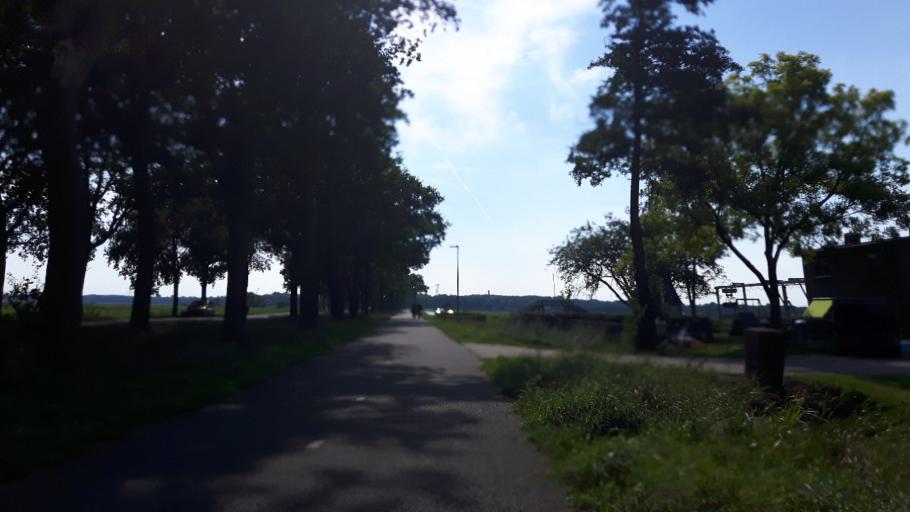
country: NL
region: Drenthe
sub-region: Gemeente Tynaarlo
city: Zuidlaren
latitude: 53.1074
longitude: 6.7058
